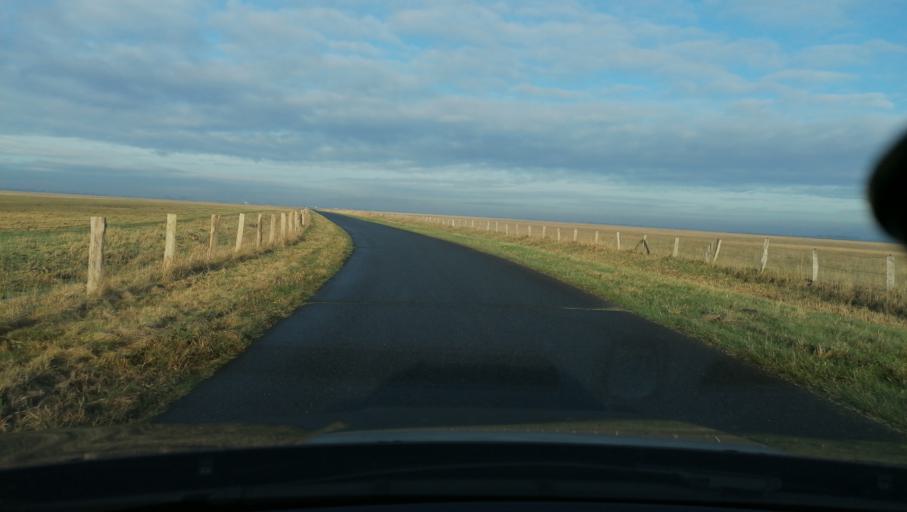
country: DE
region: Schleswig-Holstein
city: Friedrichsgabekoog
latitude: 54.1052
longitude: 8.9535
